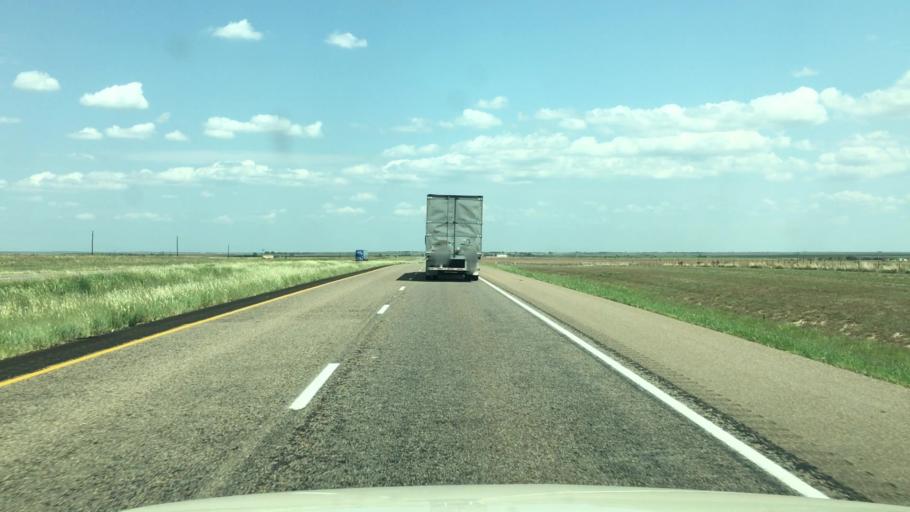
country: US
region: Texas
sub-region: Armstrong County
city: Claude
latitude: 35.0322
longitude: -101.1377
